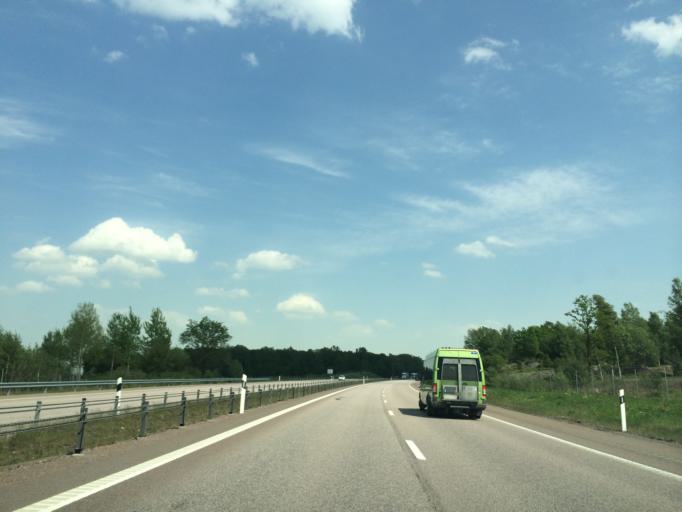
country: SE
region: OEstergoetland
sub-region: Odeshogs Kommun
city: OEdeshoeg
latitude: 58.2369
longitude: 14.7135
